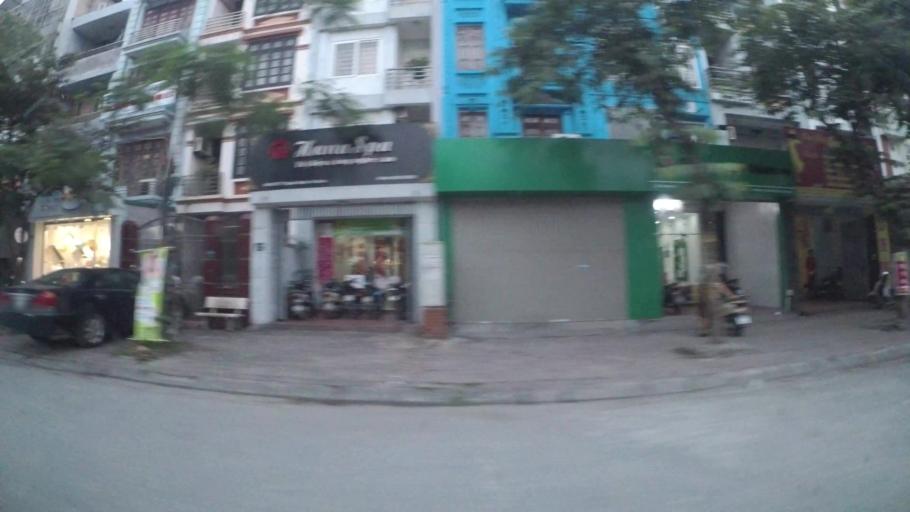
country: VN
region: Ha Noi
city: Ha Dong
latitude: 20.9718
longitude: 105.7904
